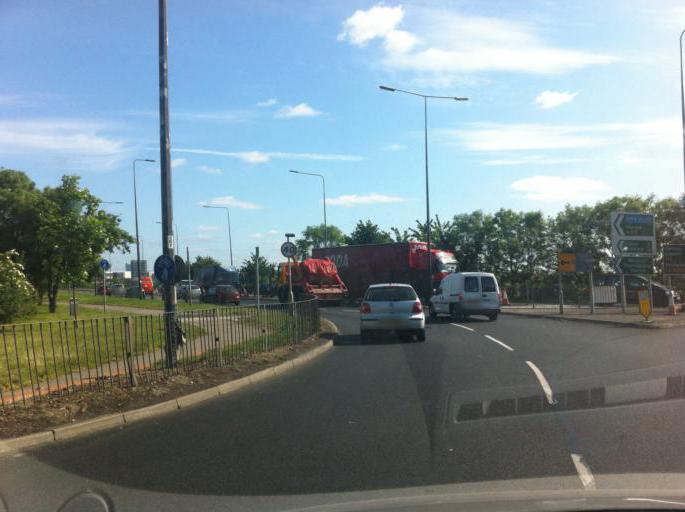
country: GB
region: England
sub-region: Greater London
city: Feltham
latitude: 51.4753
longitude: -0.4050
